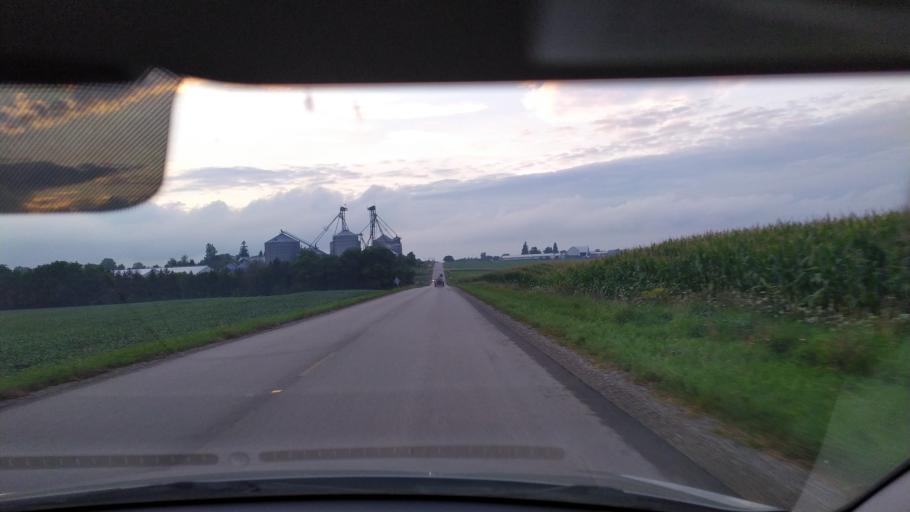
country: CA
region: Ontario
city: Kitchener
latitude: 43.3321
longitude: -80.6229
